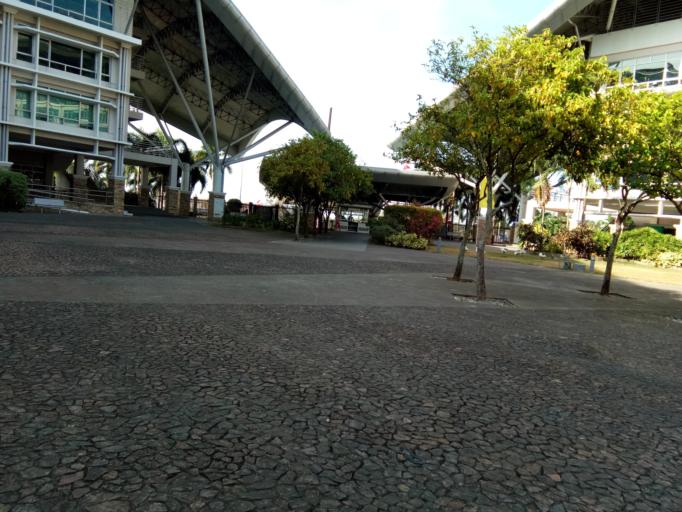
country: PH
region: Calabarzon
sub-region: Province of Cavite
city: Manggahan
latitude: 14.2911
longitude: 120.9154
